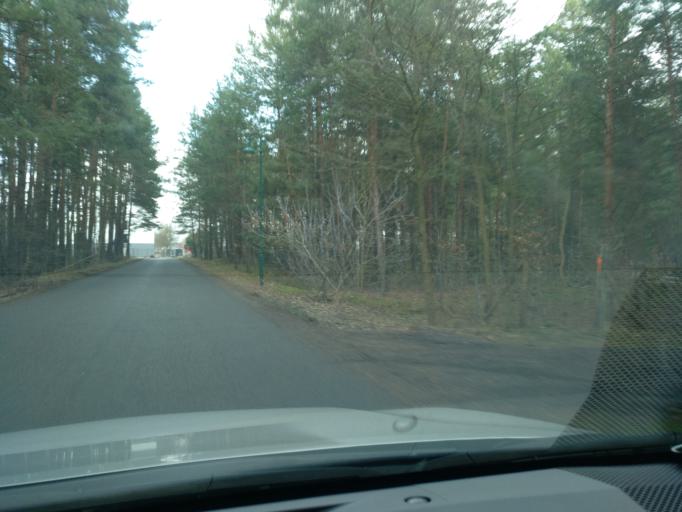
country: DE
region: Brandenburg
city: Grunheide
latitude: 52.3805
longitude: 13.7997
